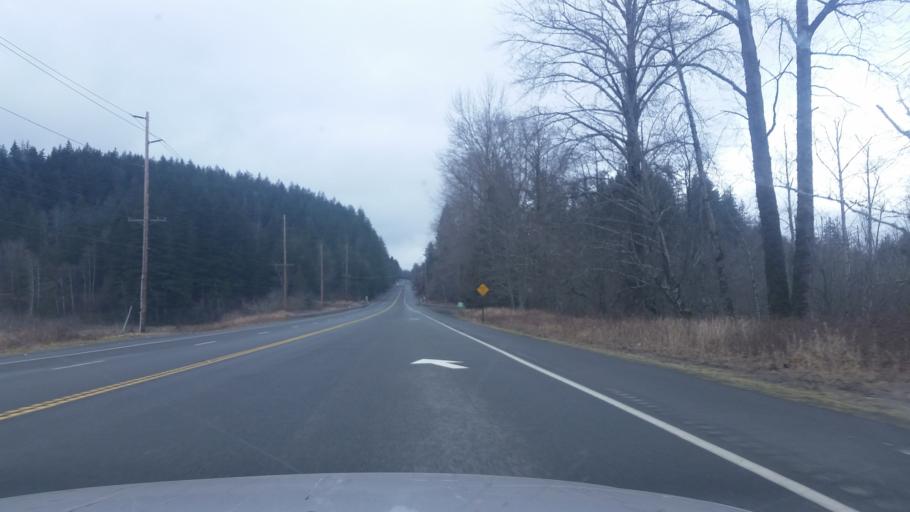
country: US
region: Washington
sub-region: King County
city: Snoqualmie
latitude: 47.5087
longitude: -121.8169
